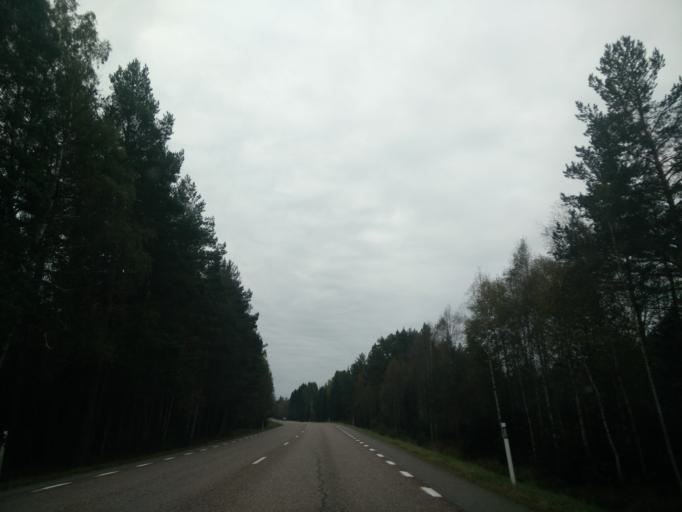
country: SE
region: Gaevleborg
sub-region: Gavle Kommun
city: Norrsundet
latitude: 60.8457
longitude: 17.1982
